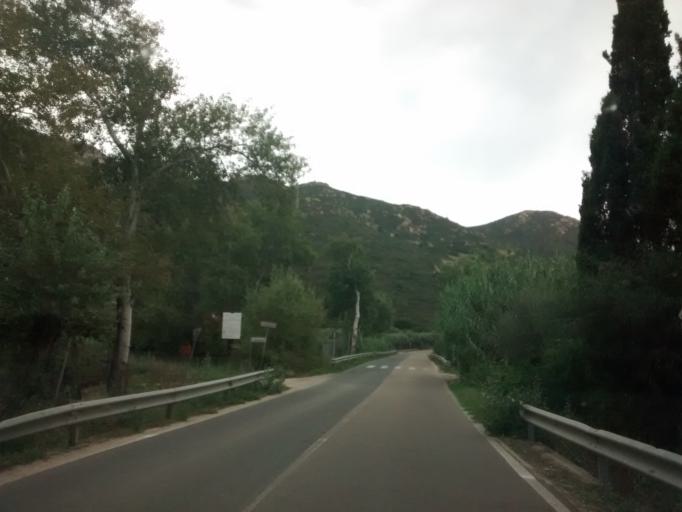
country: IT
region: Sardinia
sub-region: Provincia di Cagliari
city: Villasimius
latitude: 39.1389
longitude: 9.4376
